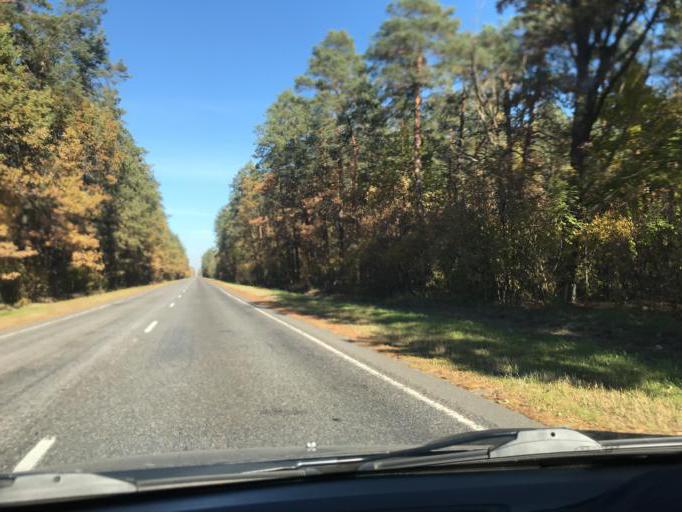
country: BY
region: Gomel
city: Kalinkavichy
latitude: 52.2501
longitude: 29.3127
